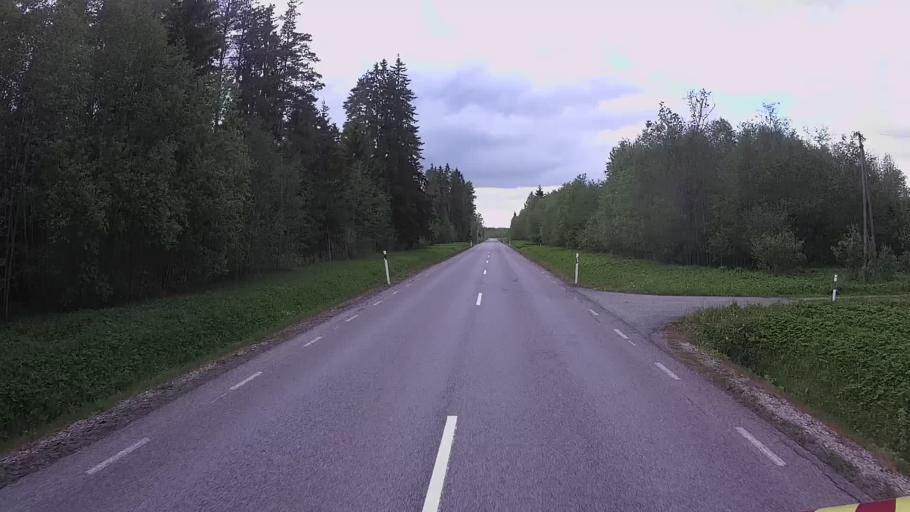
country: EE
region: Jogevamaa
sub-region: Mustvee linn
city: Mustvee
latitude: 59.0734
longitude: 26.9969
